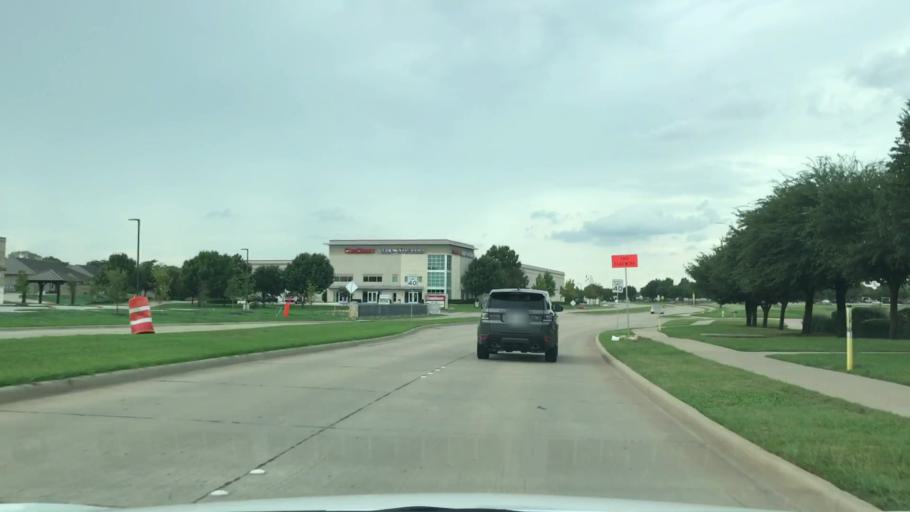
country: US
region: Texas
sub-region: Collin County
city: Frisco
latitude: 33.1284
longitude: -96.8056
